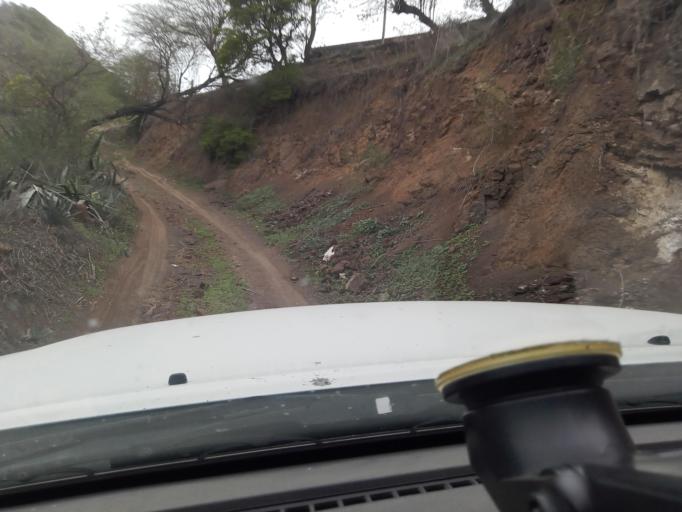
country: CV
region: Sao Salvador do Mundo
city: Picos
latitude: 15.1419
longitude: -23.6386
